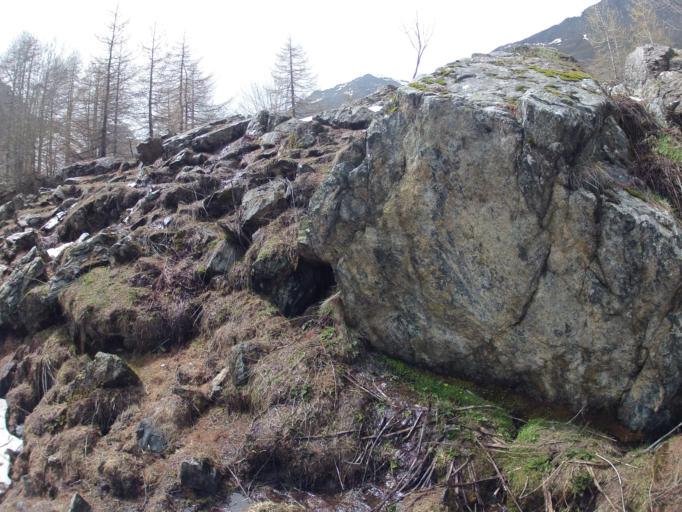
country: IT
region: Piedmont
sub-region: Provincia di Cuneo
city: Crissolo
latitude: 44.6994
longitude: 7.1254
